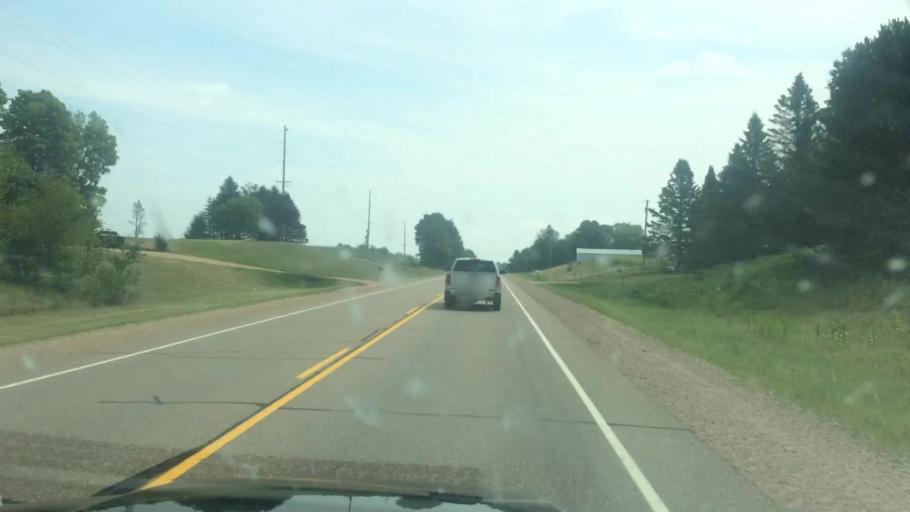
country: US
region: Wisconsin
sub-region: Langlade County
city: Antigo
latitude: 45.1613
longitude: -89.0371
